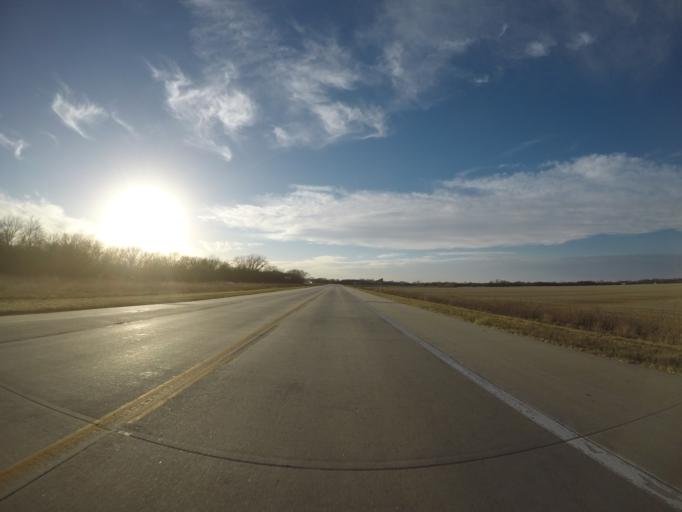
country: US
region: Kansas
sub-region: Chase County
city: Cottonwood Falls
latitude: 38.4069
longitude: -96.3745
